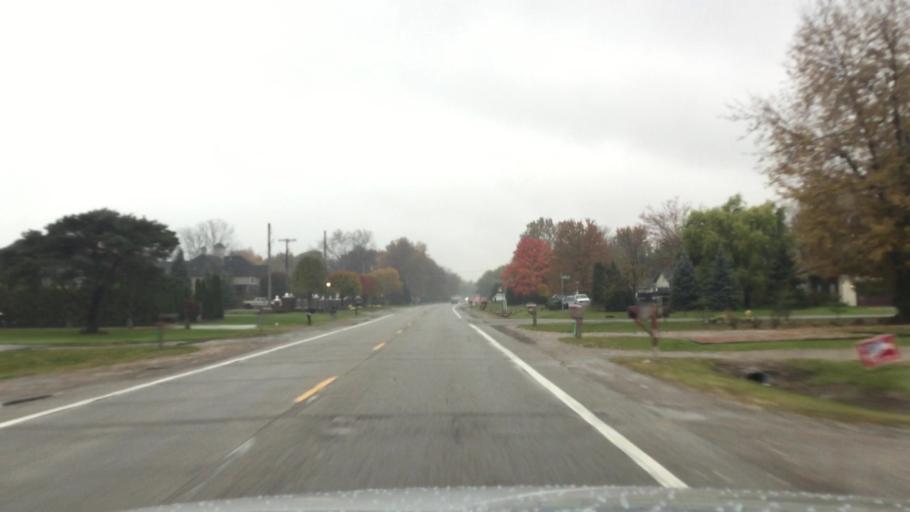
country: US
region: Michigan
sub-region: Macomb County
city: New Baltimore
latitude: 42.6528
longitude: -82.8036
